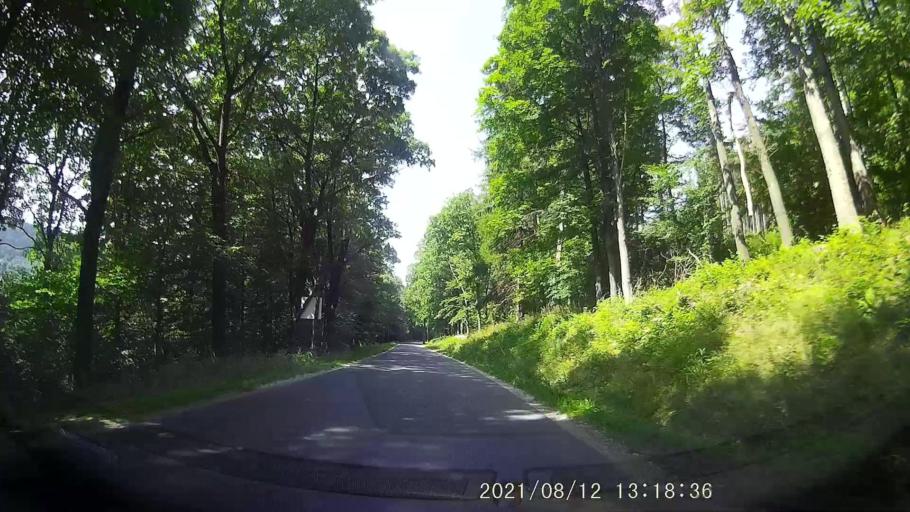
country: PL
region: Lower Silesian Voivodeship
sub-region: Powiat klodzki
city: Stronie Slaskie
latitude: 50.2727
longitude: 16.8898
